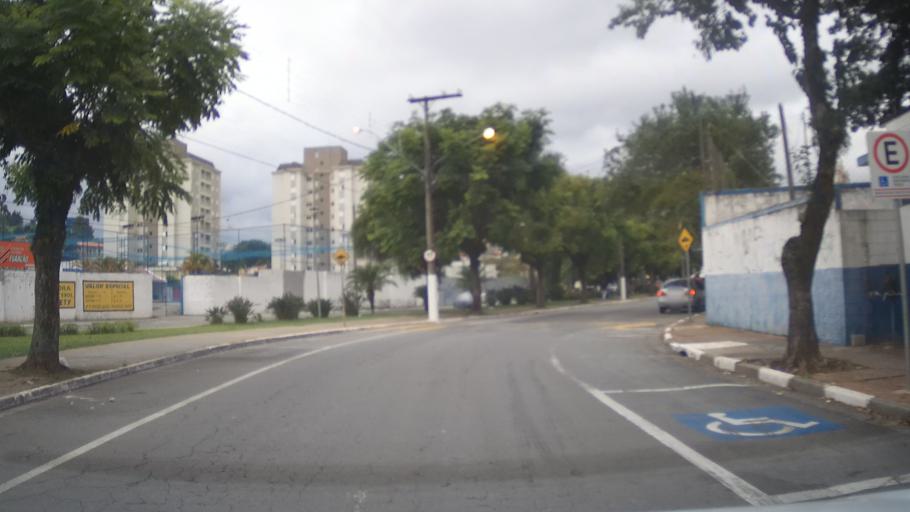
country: BR
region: Sao Paulo
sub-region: Aruja
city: Aruja
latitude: -23.3950
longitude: -46.3171
